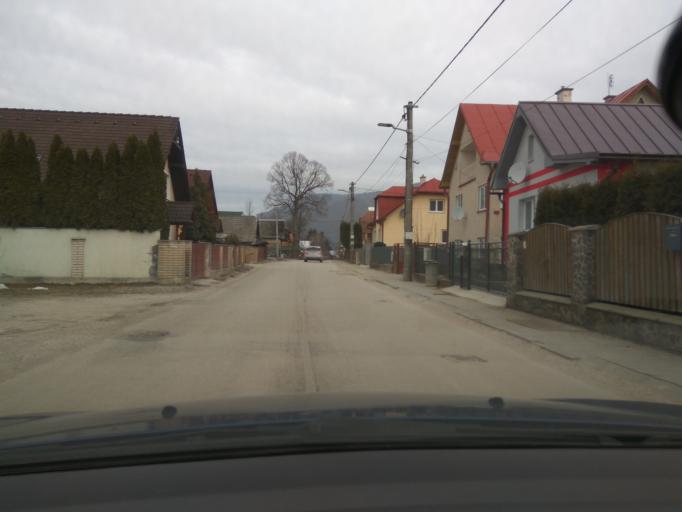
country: SK
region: Zilinsky
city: Rajec
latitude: 49.1153
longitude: 18.6773
